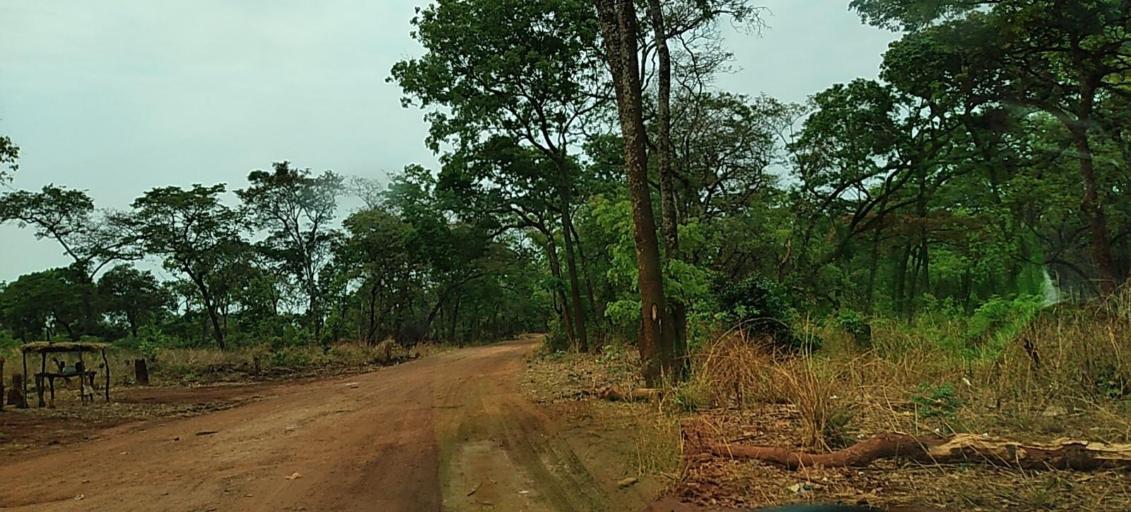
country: ZM
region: North-Western
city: Solwezi
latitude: -12.3081
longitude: 26.5226
